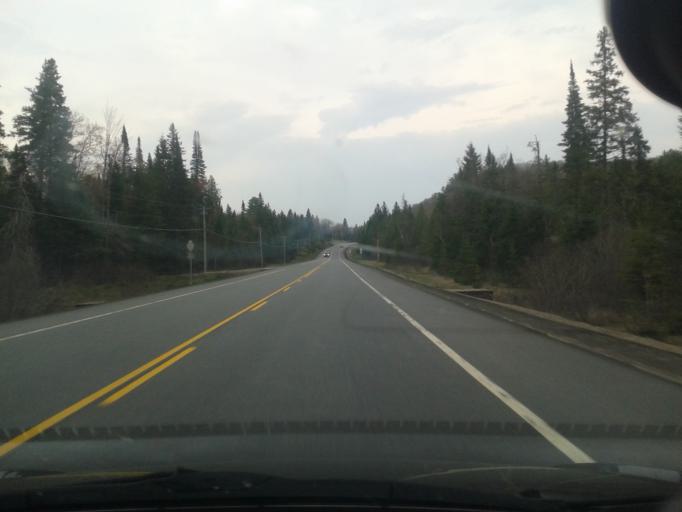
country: CA
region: Ontario
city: Huntsville
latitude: 45.4915
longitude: -78.7489
